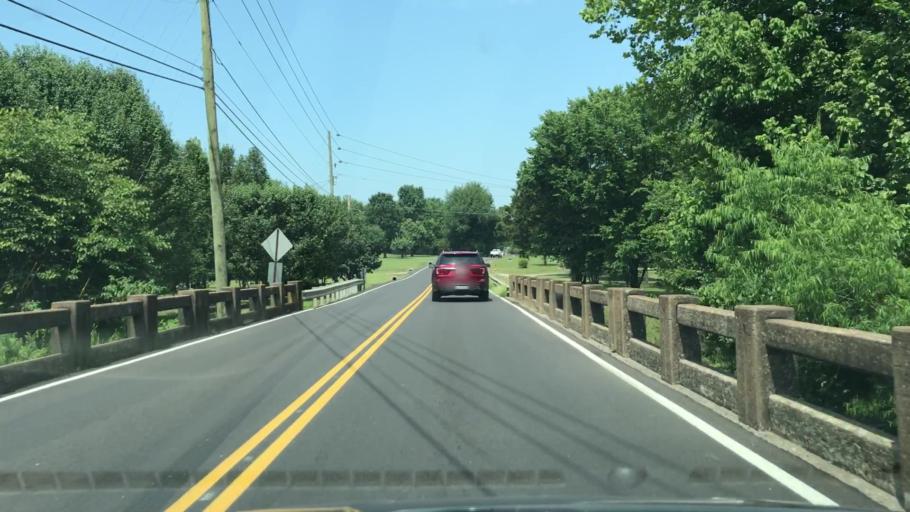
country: US
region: Tennessee
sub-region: Wilson County
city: Rural Hill
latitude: 36.1180
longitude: -86.4923
